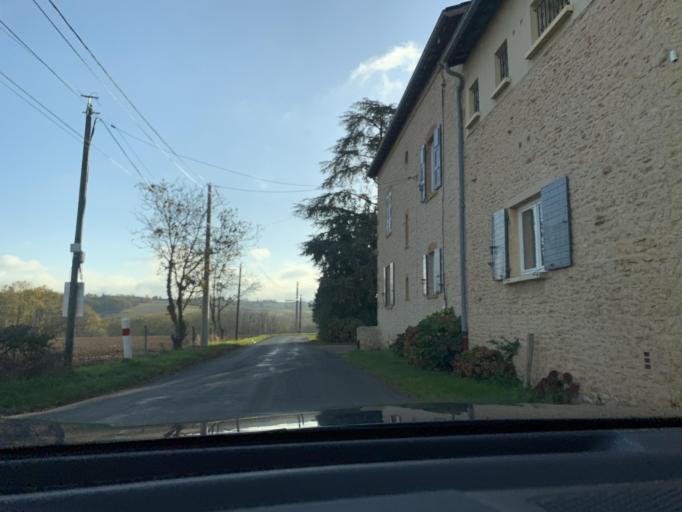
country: FR
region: Rhone-Alpes
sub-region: Departement du Rhone
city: Pommiers
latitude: 45.9481
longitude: 4.6720
